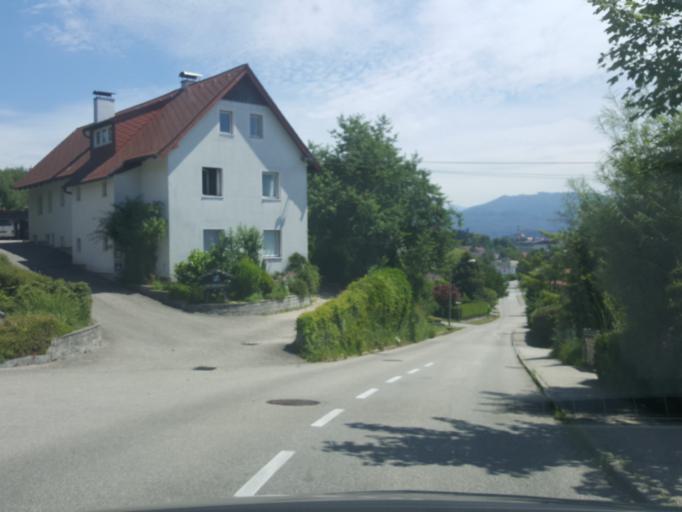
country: AT
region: Upper Austria
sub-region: Politischer Bezirk Vocklabruck
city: Seewalchen
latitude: 47.9566
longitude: 13.5810
